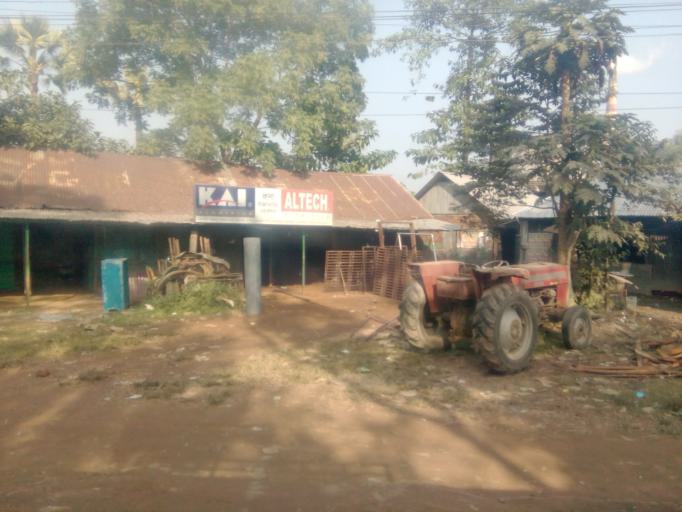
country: BD
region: Chittagong
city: Comilla
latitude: 23.4008
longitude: 91.2294
